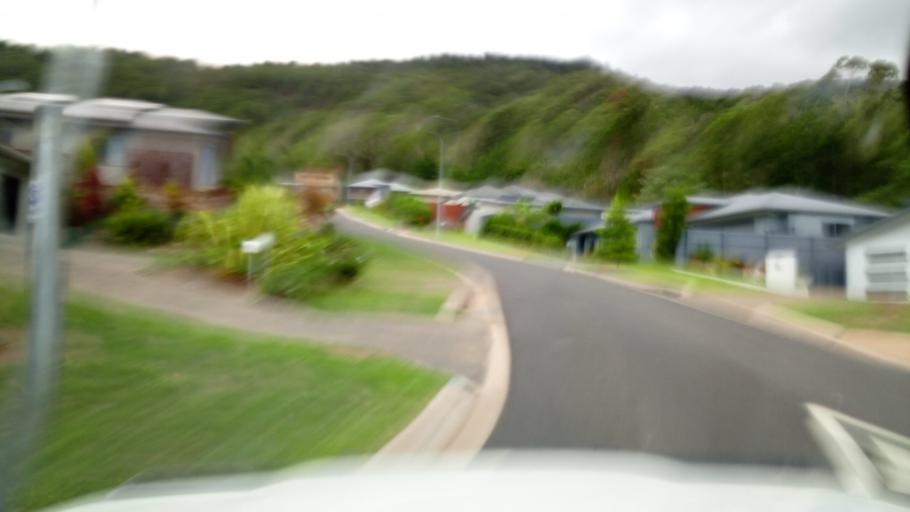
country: AU
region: Queensland
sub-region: Cairns
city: Redlynch
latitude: -16.8433
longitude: 145.6876
